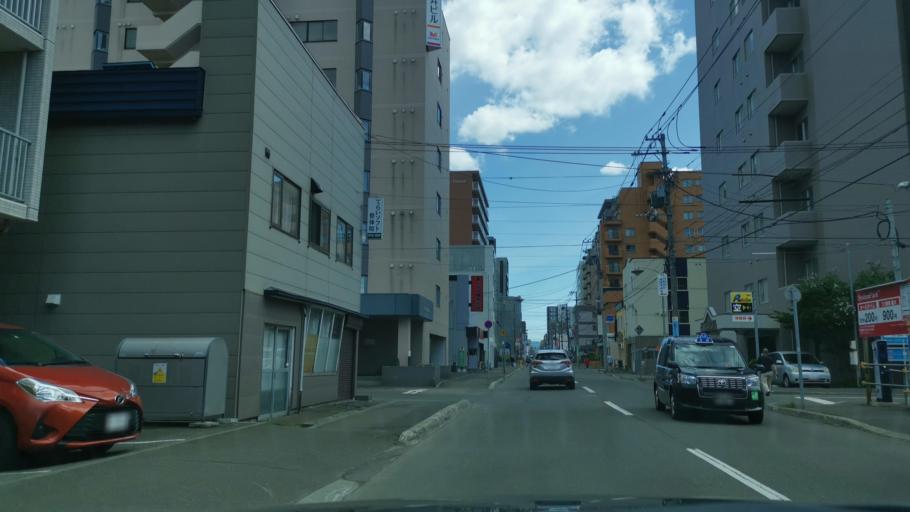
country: JP
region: Hokkaido
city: Sapporo
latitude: 43.0449
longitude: 141.3466
